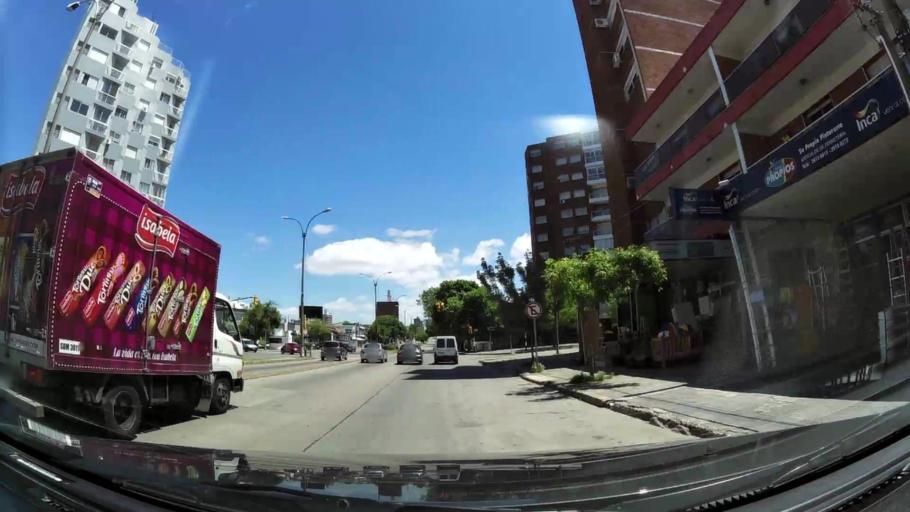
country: UY
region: Montevideo
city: Montevideo
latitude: -34.8932
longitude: -56.1294
